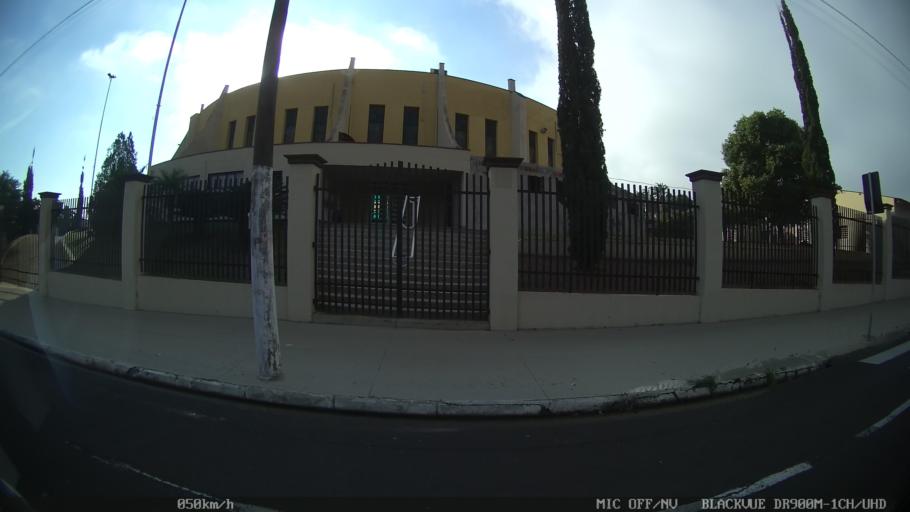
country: BR
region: Sao Paulo
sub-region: Sao Jose Do Rio Preto
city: Sao Jose do Rio Preto
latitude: -20.8299
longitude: -49.3658
